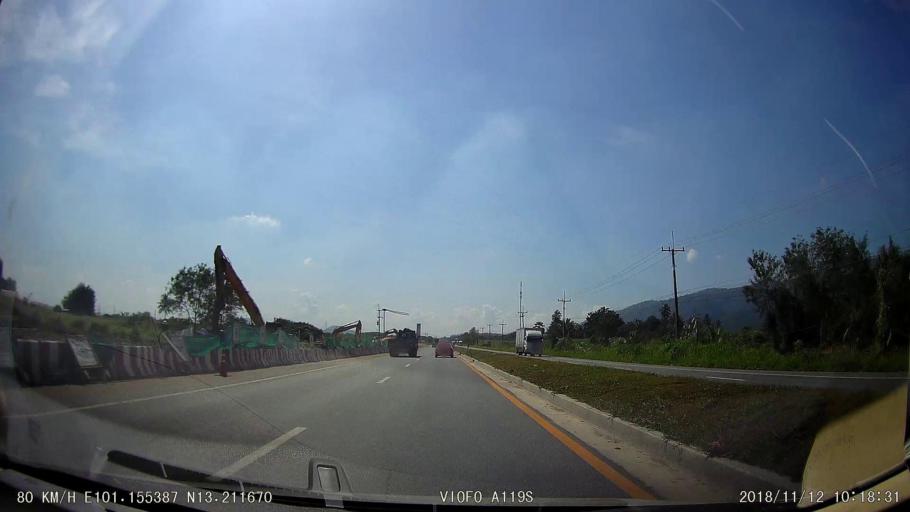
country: TH
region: Chon Buri
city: Ban Bueng
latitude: 13.2113
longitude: 101.1554
